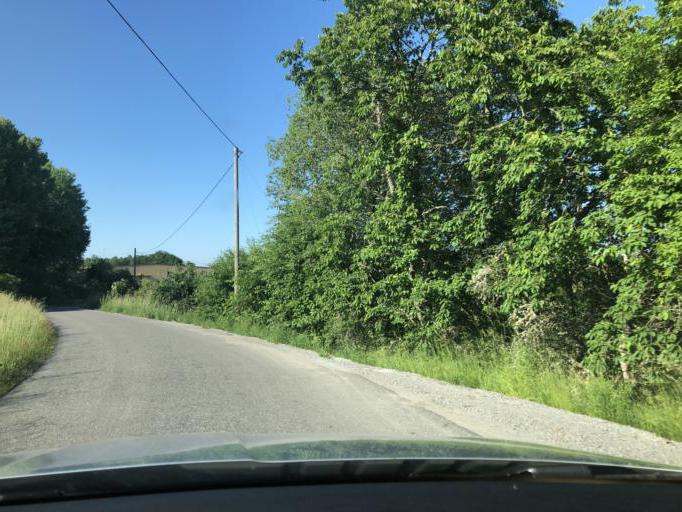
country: SE
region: Blekinge
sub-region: Karlshamns Kommun
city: Karlshamn
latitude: 56.1699
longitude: 14.8160
